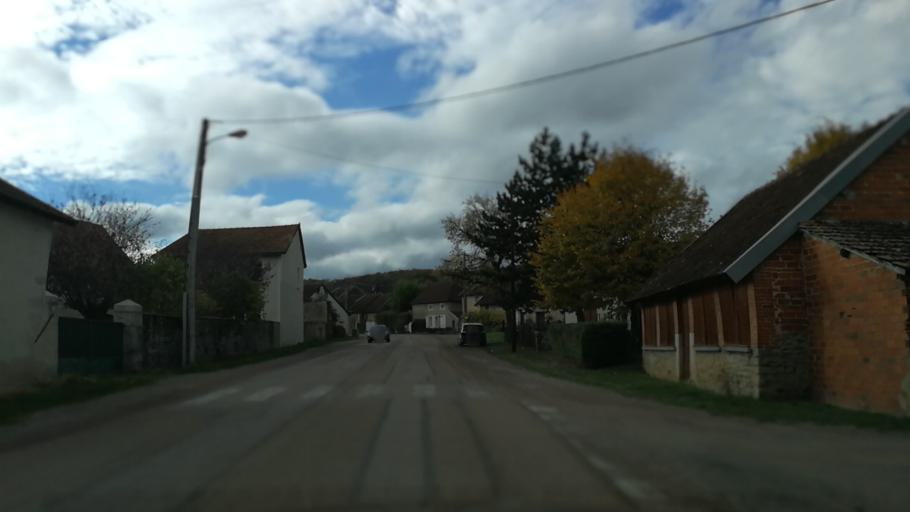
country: FR
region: Bourgogne
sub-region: Departement de la Cote-d'Or
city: Pouilly-en-Auxois
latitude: 47.2715
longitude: 4.4838
